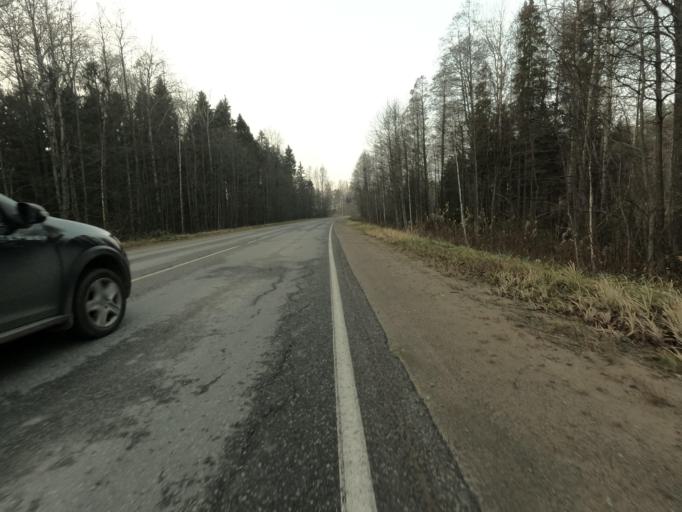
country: RU
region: Leningrad
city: Kirovsk
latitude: 59.8248
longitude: 30.9811
